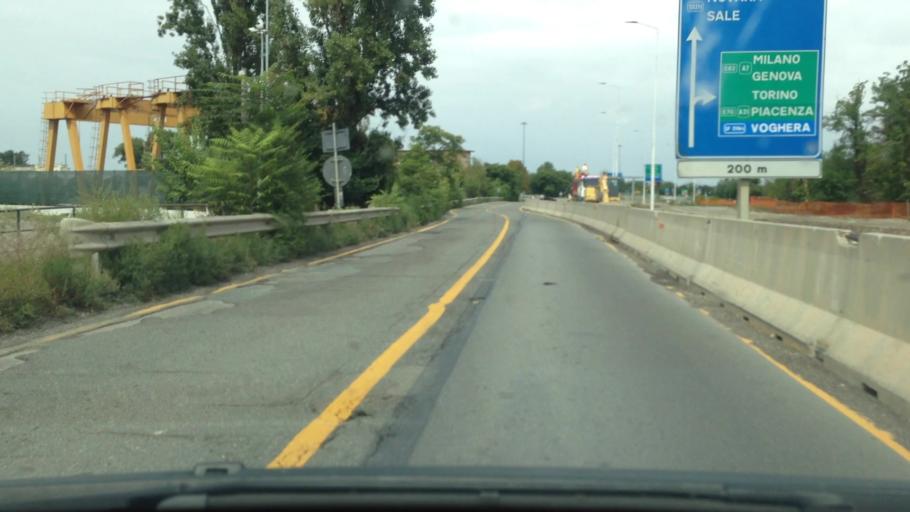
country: IT
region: Piedmont
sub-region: Provincia di Alessandria
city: Tortona
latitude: 44.9037
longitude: 8.8379
